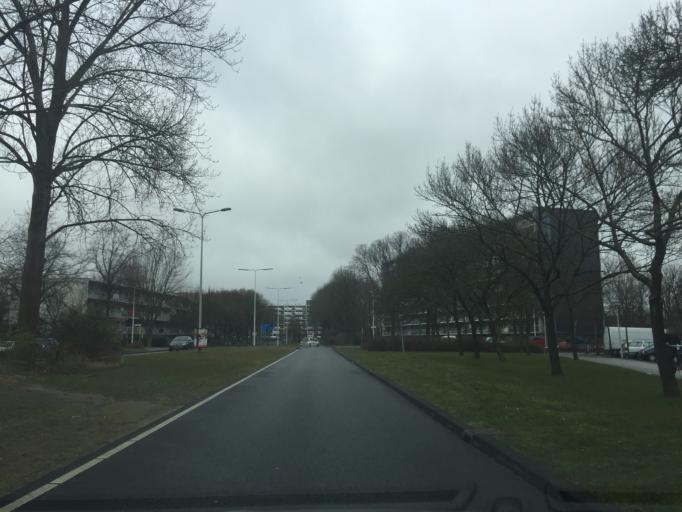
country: NL
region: South Holland
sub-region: Gemeente Leiden
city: Leiden
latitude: 52.1723
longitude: 4.5101
